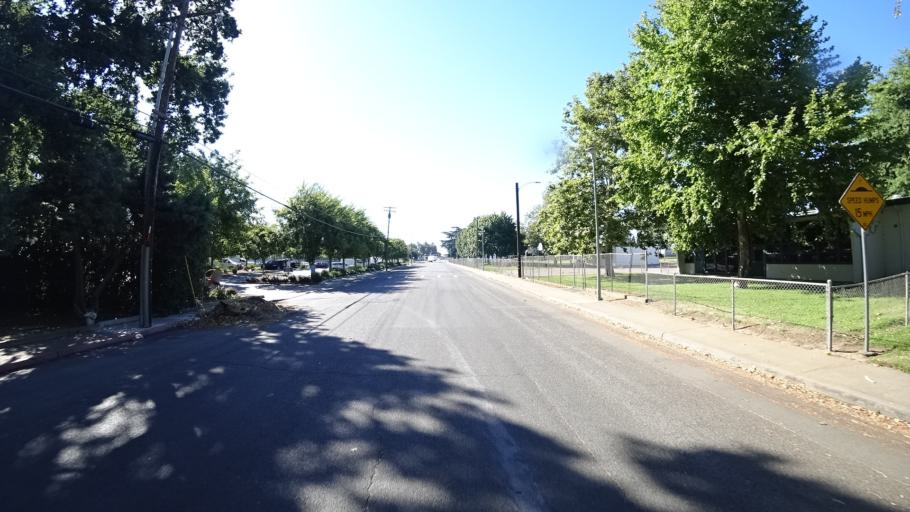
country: US
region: California
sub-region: Sacramento County
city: Sacramento
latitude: 38.5970
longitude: -121.4824
